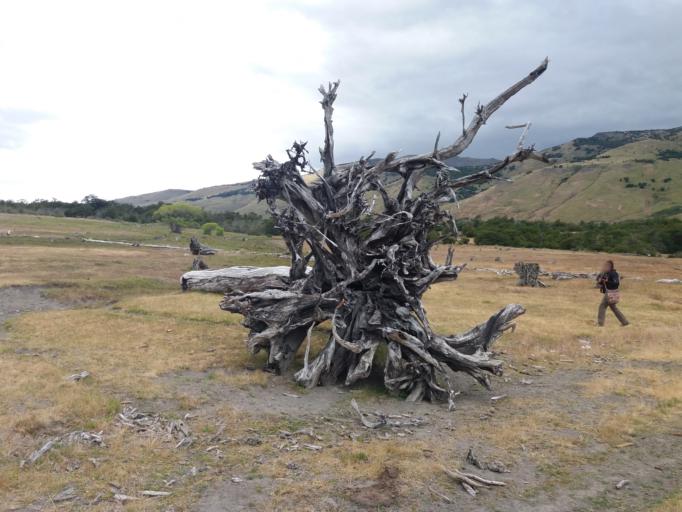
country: AR
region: Santa Cruz
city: El Calafate
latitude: -50.5543
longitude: -72.8494
